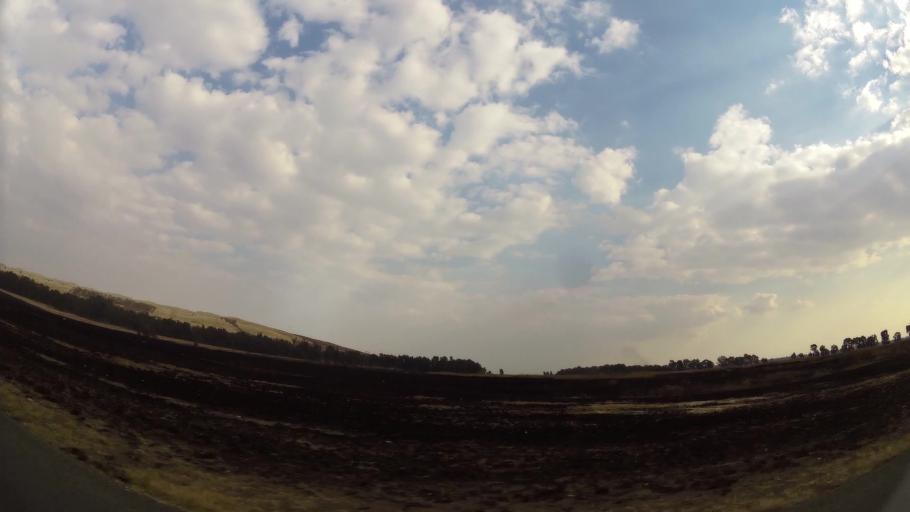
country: ZA
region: Gauteng
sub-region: Ekurhuleni Metropolitan Municipality
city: Springs
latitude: -26.2833
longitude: 28.5290
